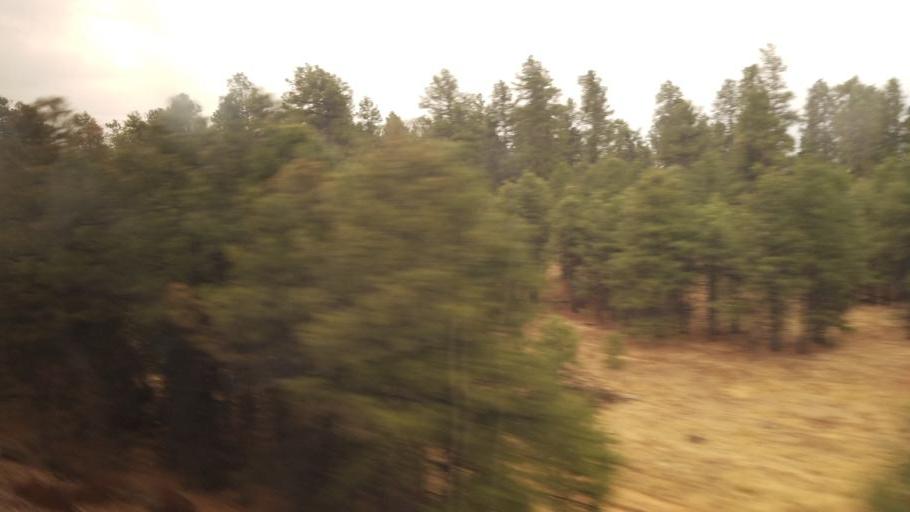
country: US
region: Arizona
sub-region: Coconino County
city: Parks
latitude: 35.2437
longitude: -111.8795
